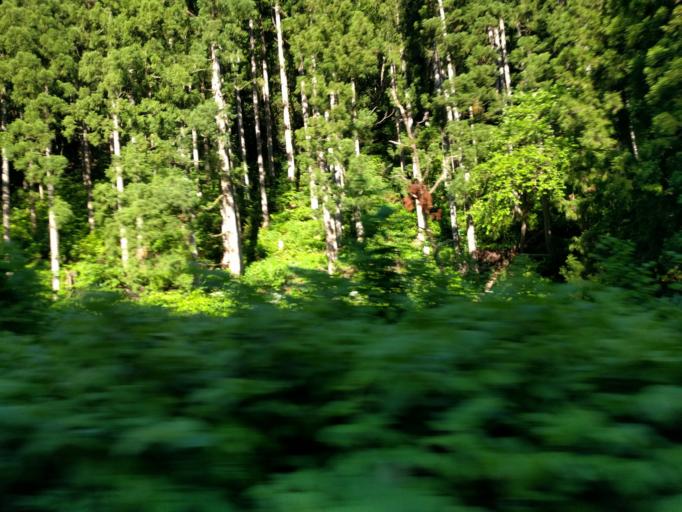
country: JP
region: Fukushima
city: Kitakata
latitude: 37.3695
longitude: 139.8096
